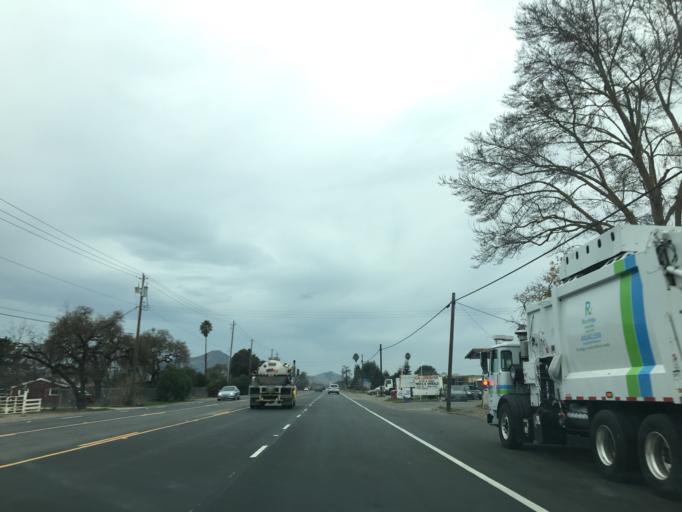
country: US
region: California
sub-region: Santa Clara County
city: San Martin
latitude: 37.1007
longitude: -121.6240
